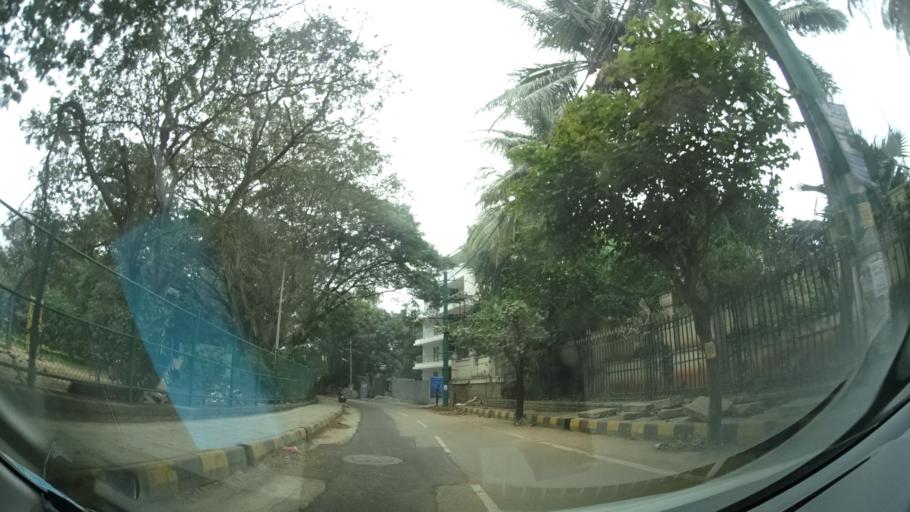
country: IN
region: Karnataka
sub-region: Bangalore Rural
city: Hoskote
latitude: 12.9722
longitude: 77.7485
